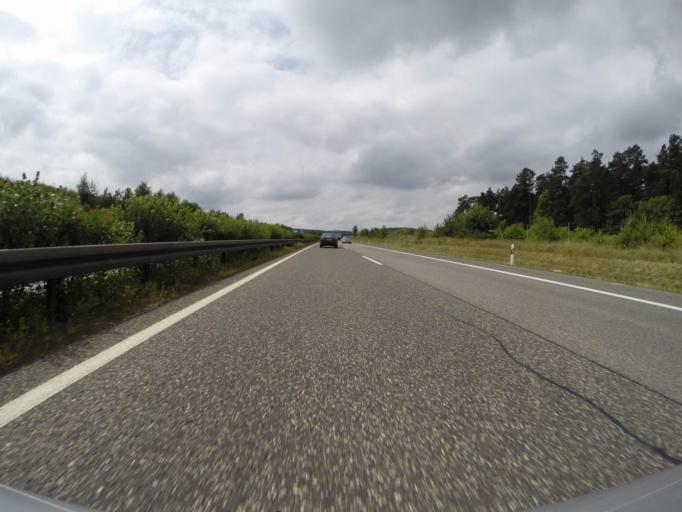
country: DE
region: Thuringia
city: Langewiesen
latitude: 50.7231
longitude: 10.9765
